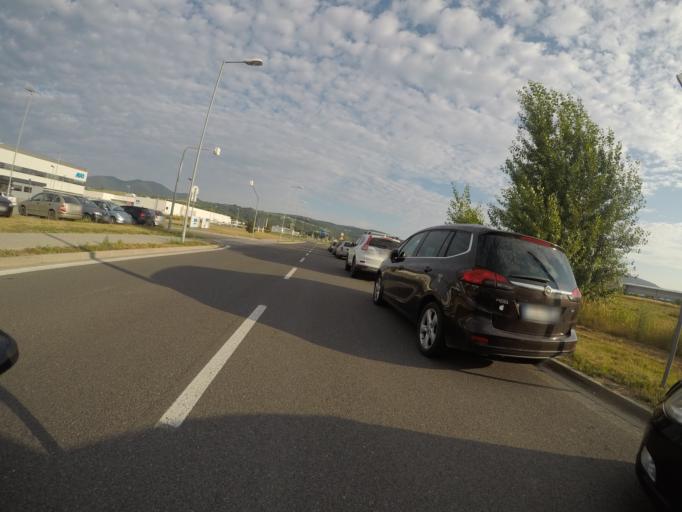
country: SK
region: Trenciansky
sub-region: Okres Trencin
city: Trencin
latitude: 48.8879
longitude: 17.9995
